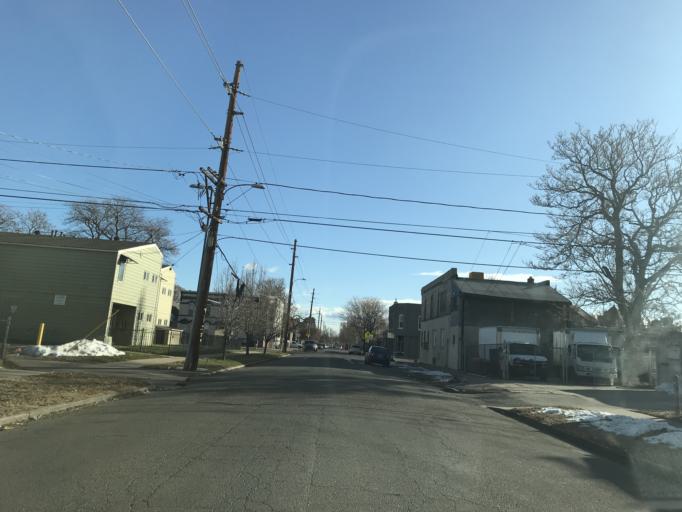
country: US
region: Colorado
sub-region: Denver County
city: Denver
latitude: 39.7682
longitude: -104.9706
